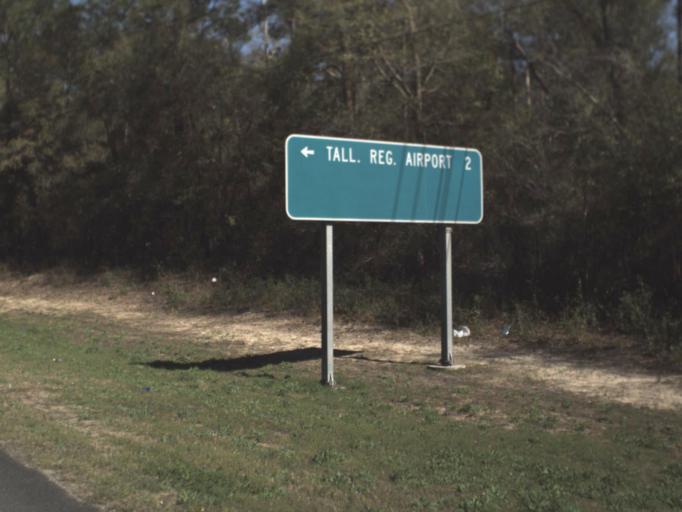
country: US
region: Florida
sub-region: Leon County
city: Tallahassee
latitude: 30.4167
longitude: -84.3467
